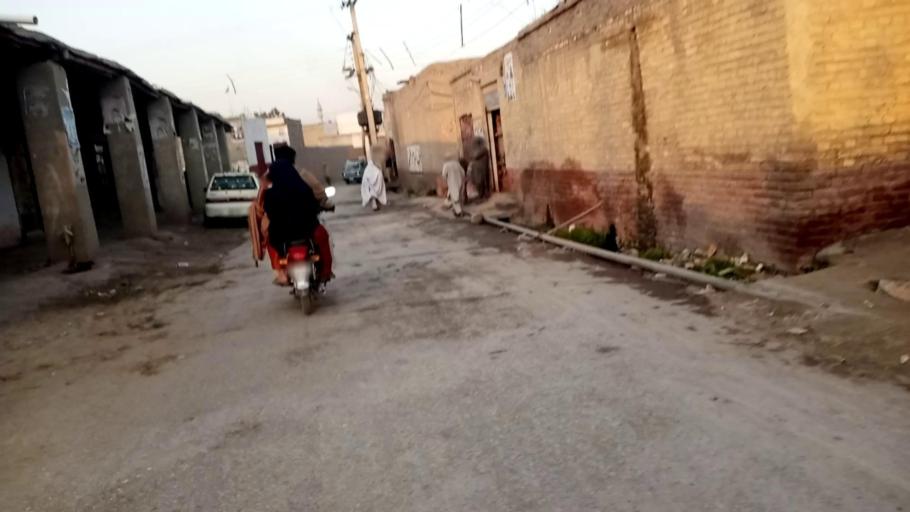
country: PK
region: Khyber Pakhtunkhwa
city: Peshawar
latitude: 34.0495
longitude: 71.4578
